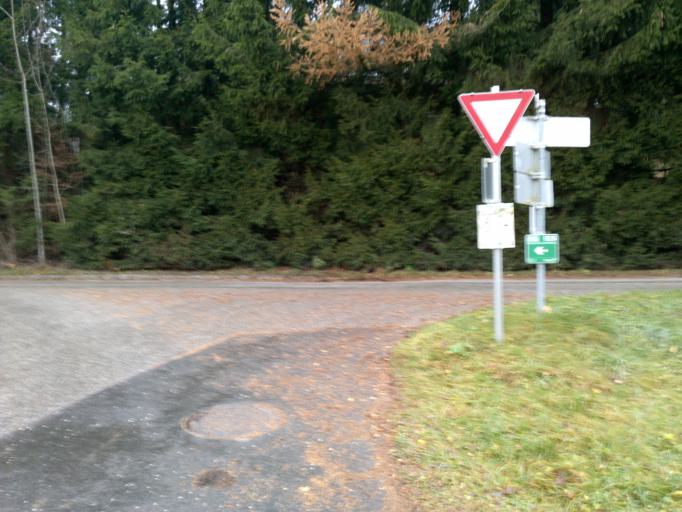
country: AT
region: Styria
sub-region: Politischer Bezirk Murtal
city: Sankt Marein bei Knittelfeld
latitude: 47.2824
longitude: 14.8708
